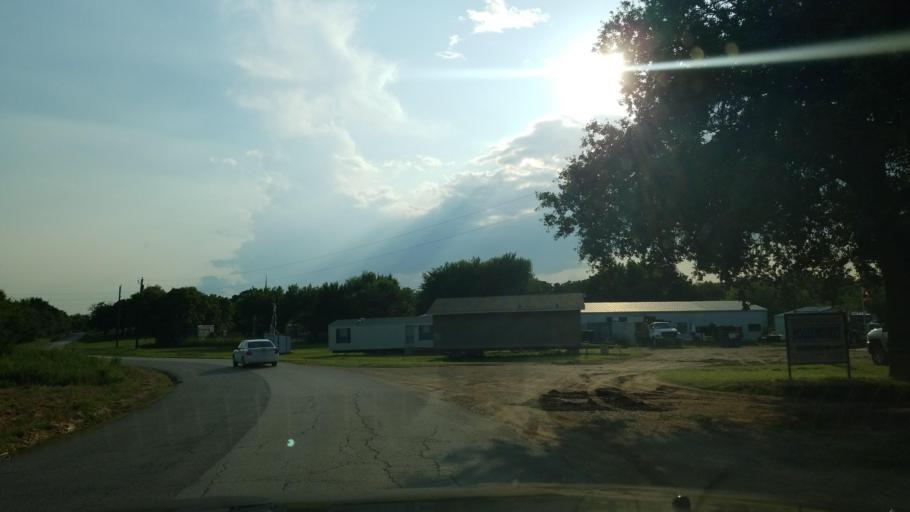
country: US
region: Texas
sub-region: Denton County
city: Denton
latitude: 33.2413
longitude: -97.0759
